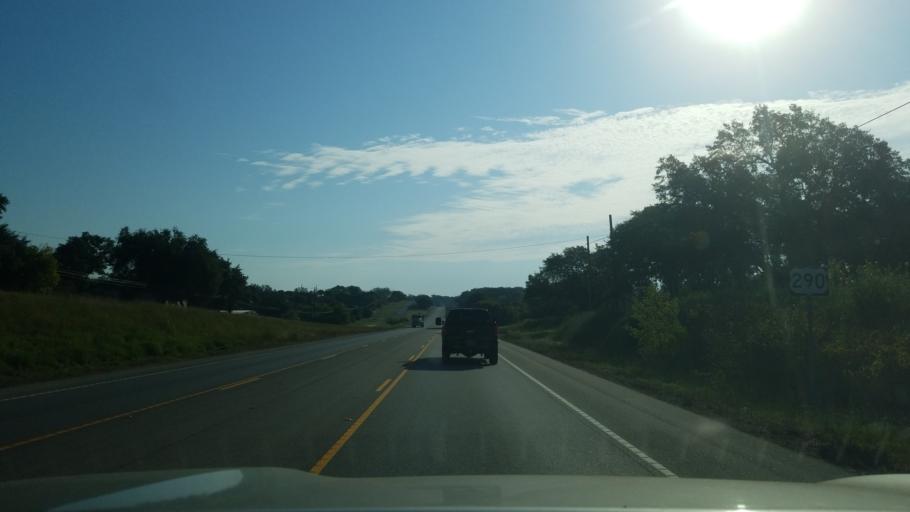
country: US
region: Texas
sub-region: Hays County
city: Dripping Springs
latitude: 30.1968
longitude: -98.1725
